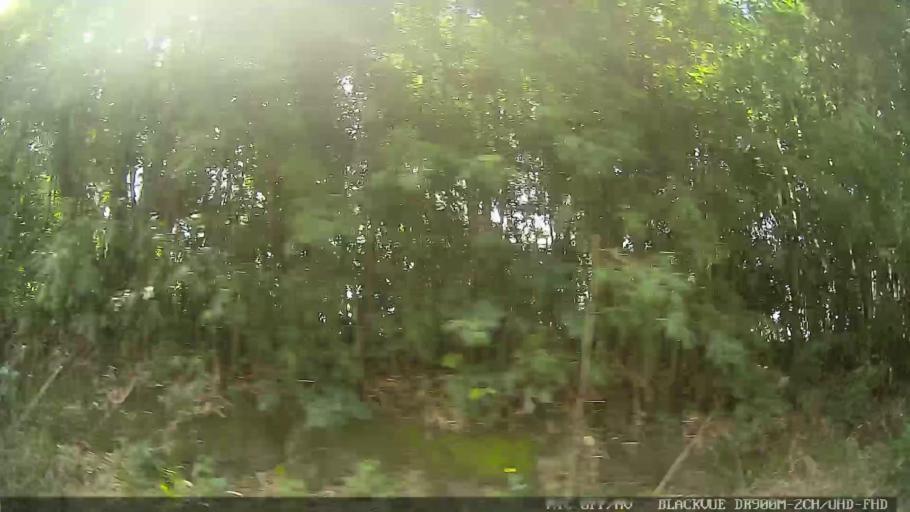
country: BR
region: Sao Paulo
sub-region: Suzano
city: Suzano
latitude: -23.4881
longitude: -46.2774
